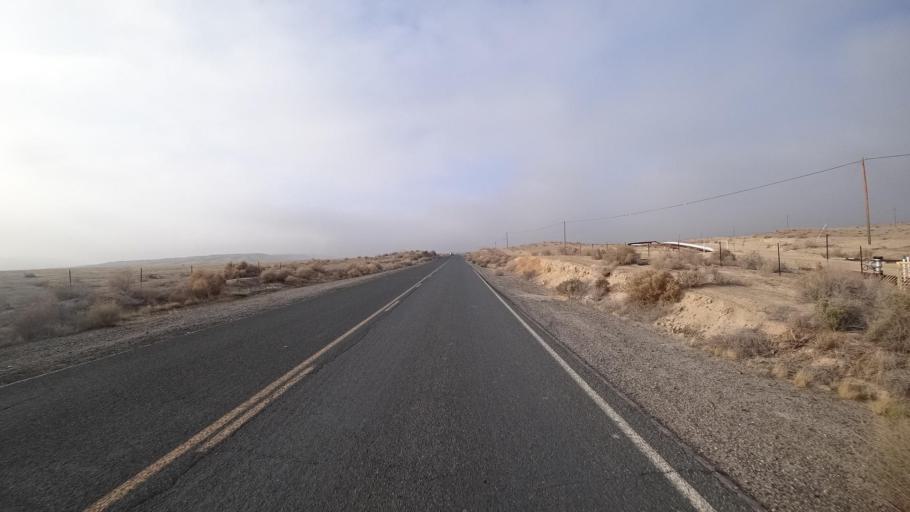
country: US
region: California
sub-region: Kern County
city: Ford City
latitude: 35.2388
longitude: -119.4494
